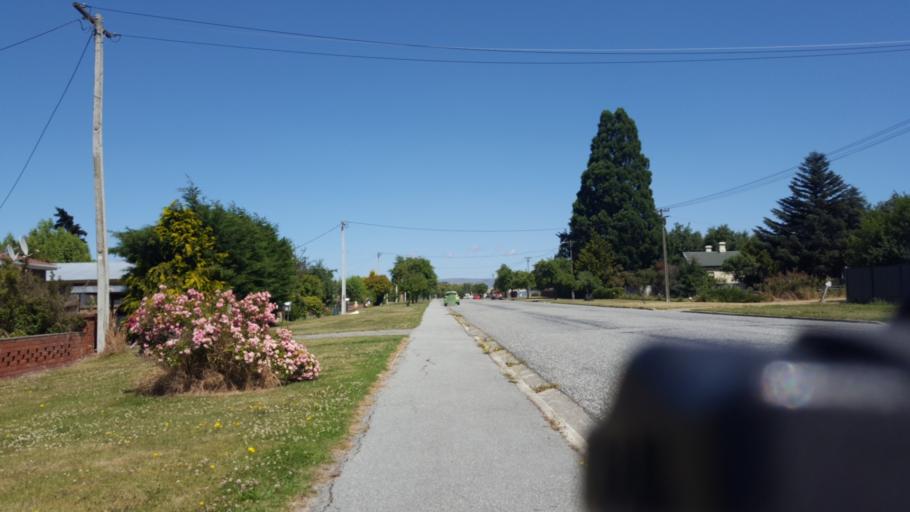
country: NZ
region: Otago
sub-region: Dunedin City
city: Dunedin
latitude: -45.1269
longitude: 170.1042
